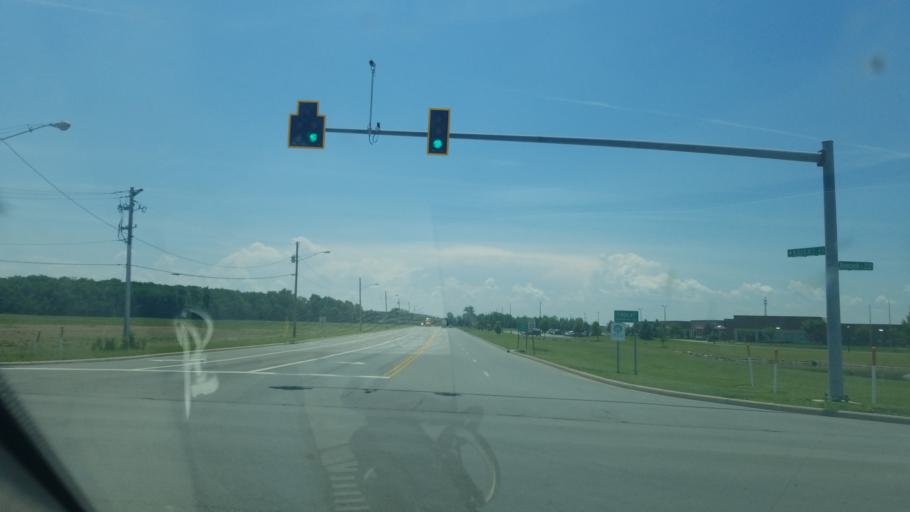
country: US
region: Ohio
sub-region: Hancock County
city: Findlay
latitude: 41.0806
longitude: -83.6181
